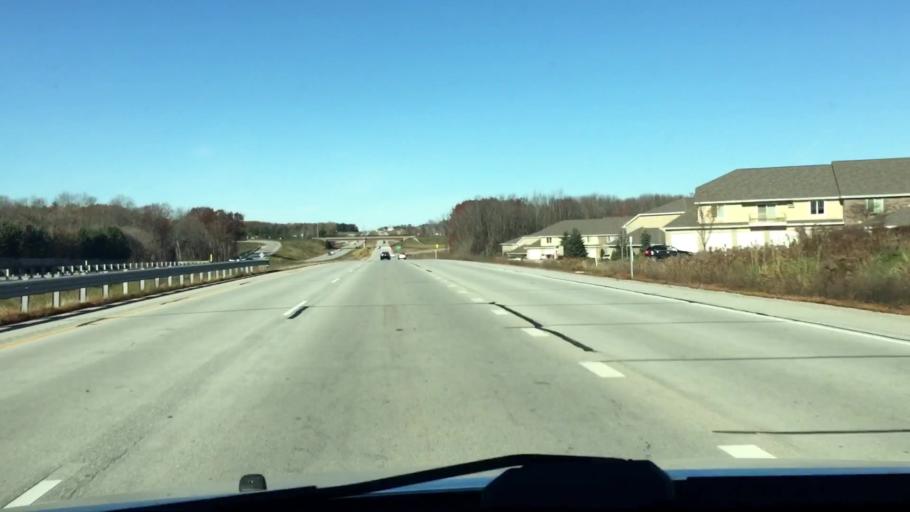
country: US
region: Wisconsin
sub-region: Brown County
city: Howard
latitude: 44.5574
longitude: -88.1224
